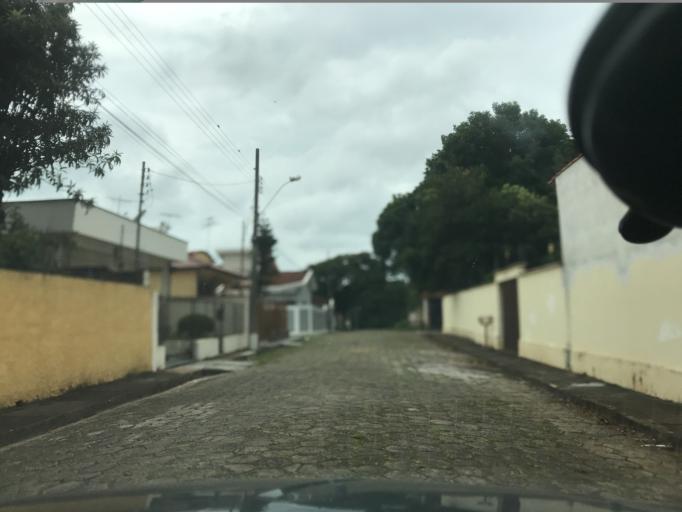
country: BR
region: Minas Gerais
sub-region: Tres Coracoes
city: Tres Coracoes
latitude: -21.6998
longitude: -45.2500
